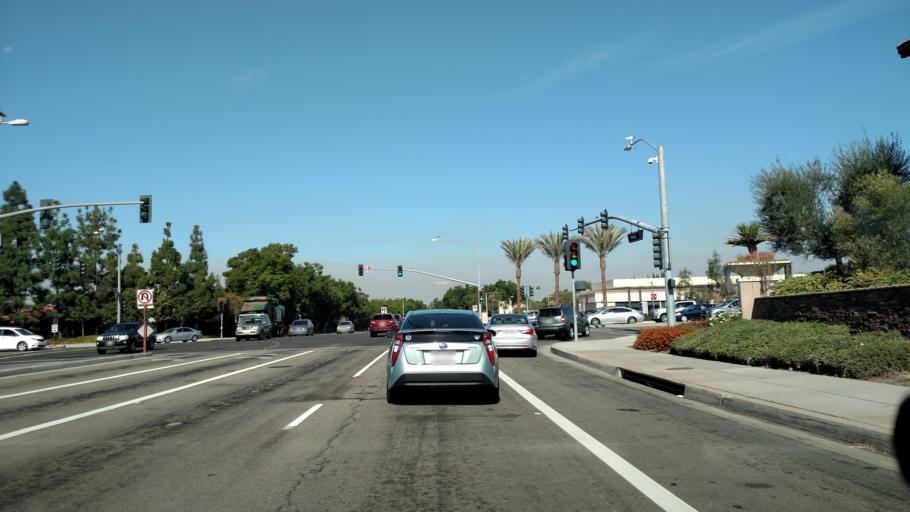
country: US
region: California
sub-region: Orange County
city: Irvine
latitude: 33.7045
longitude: -117.7871
